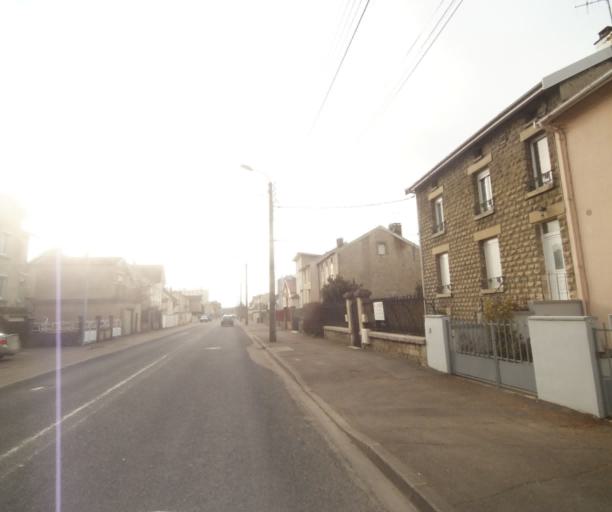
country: FR
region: Champagne-Ardenne
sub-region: Departement de la Haute-Marne
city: Saint-Dizier
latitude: 48.6409
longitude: 4.9333
